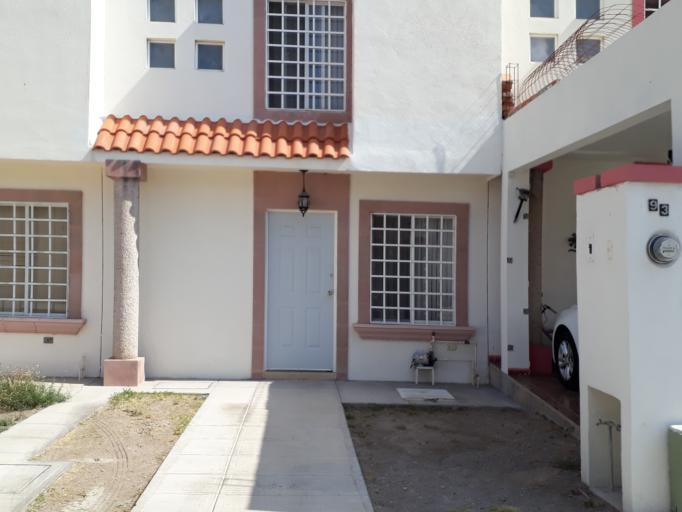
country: MX
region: Aguascalientes
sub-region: Aguascalientes
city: San Sebastian [Fraccionamiento]
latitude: 21.8077
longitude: -102.2939
